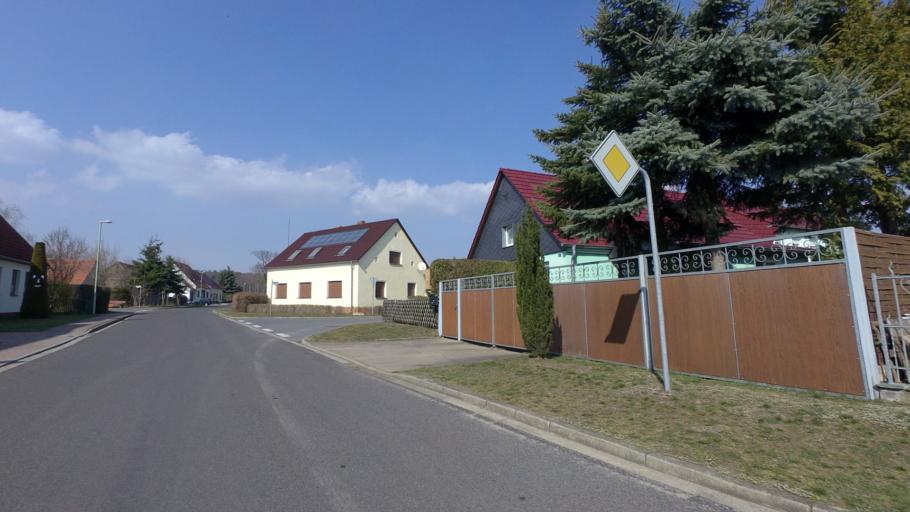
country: DE
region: Brandenburg
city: Dahme
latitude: 51.9053
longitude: 13.4865
